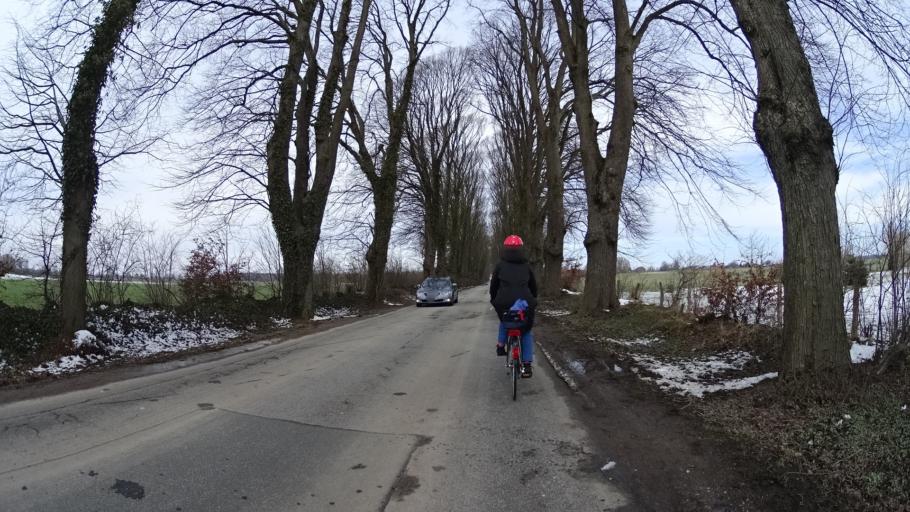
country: DE
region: Schleswig-Holstein
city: Rendswuhren
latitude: 54.0750
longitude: 10.1973
